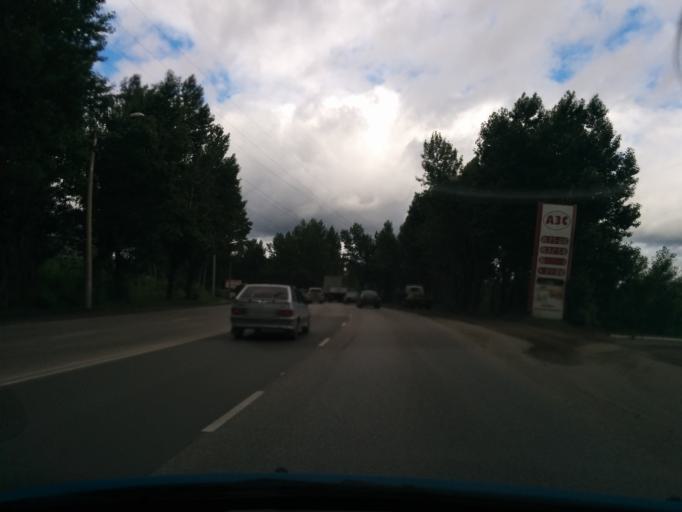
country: RU
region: Perm
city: Kondratovo
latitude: 58.0426
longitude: 56.0525
